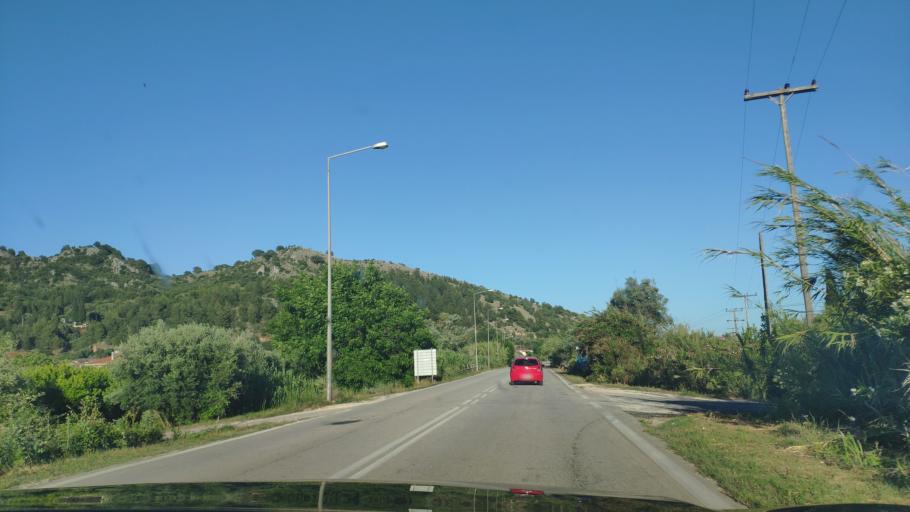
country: GR
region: Epirus
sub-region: Nomos Prevezis
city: Louros
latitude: 39.1787
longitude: 20.7850
